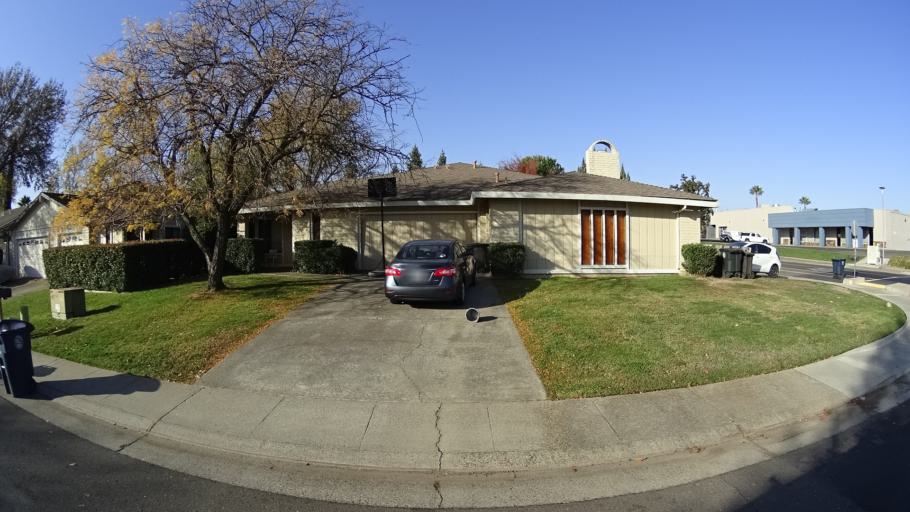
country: US
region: California
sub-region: Sacramento County
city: Citrus Heights
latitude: 38.6917
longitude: -121.2690
